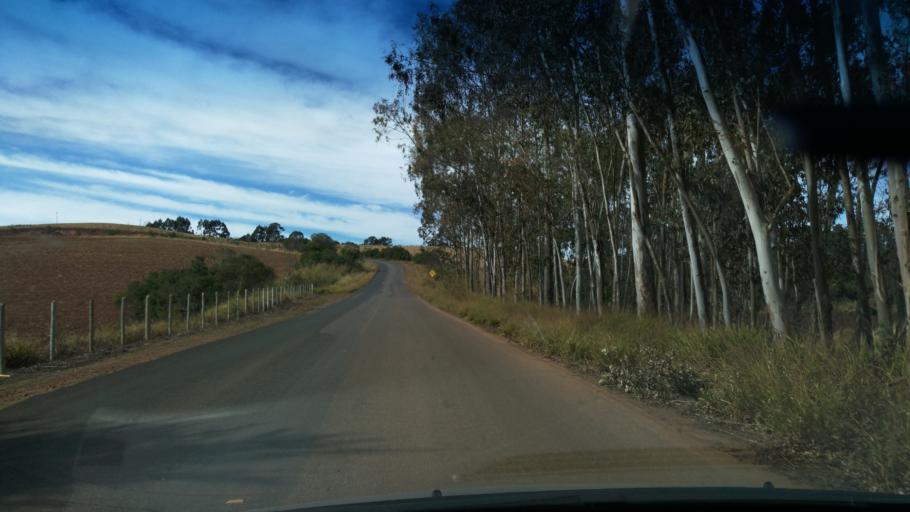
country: BR
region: Minas Gerais
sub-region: Andradas
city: Andradas
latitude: -22.0429
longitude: -46.3437
